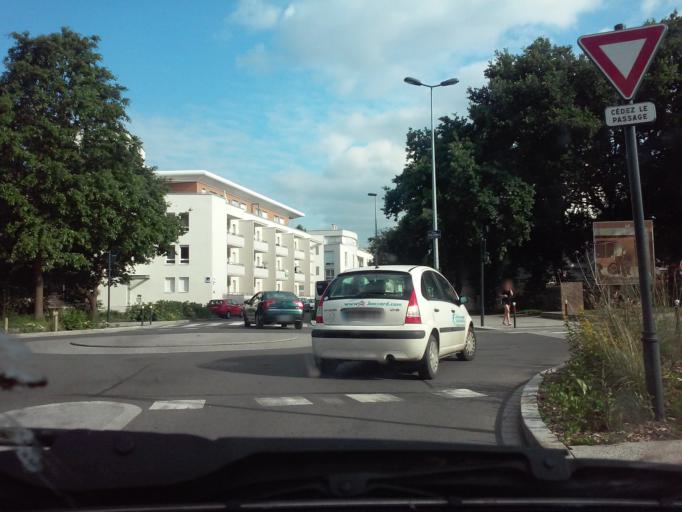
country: FR
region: Brittany
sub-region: Departement d'Ille-et-Vilaine
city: Saint-Jacques-de-la-Lande
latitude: 48.1010
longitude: -1.7118
